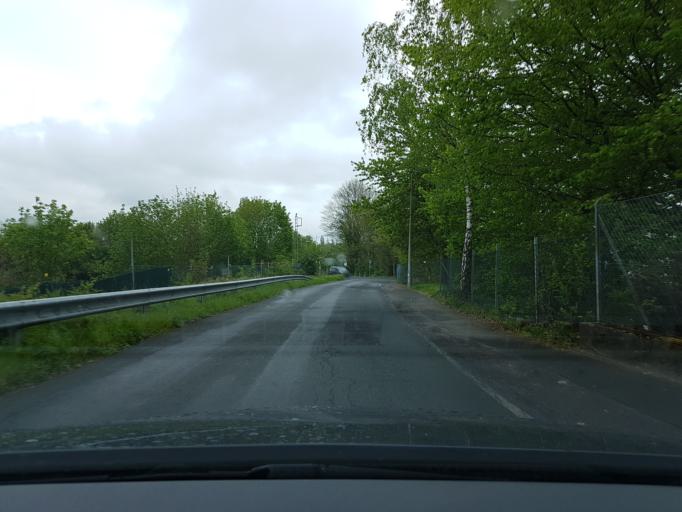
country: DE
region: Lower Saxony
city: Hameln
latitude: 52.1046
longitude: 9.3922
